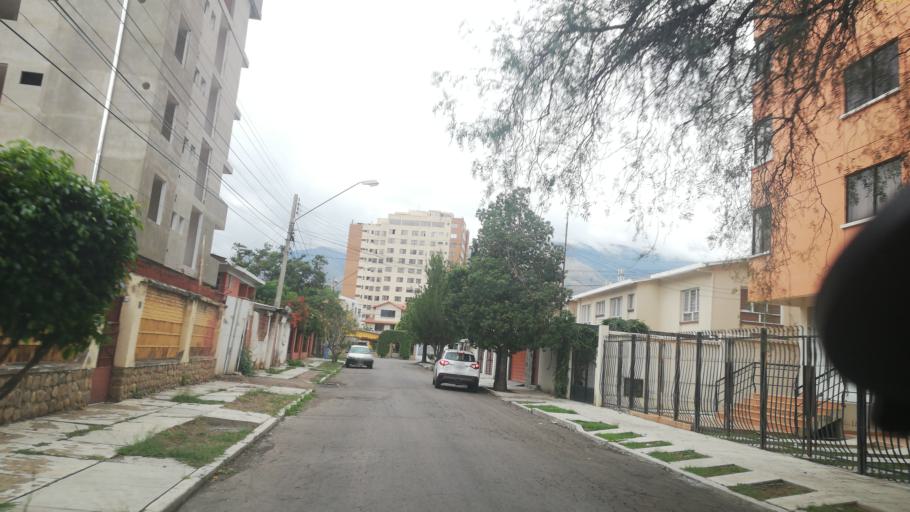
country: BO
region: Cochabamba
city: Cochabamba
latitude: -17.3744
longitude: -66.1669
